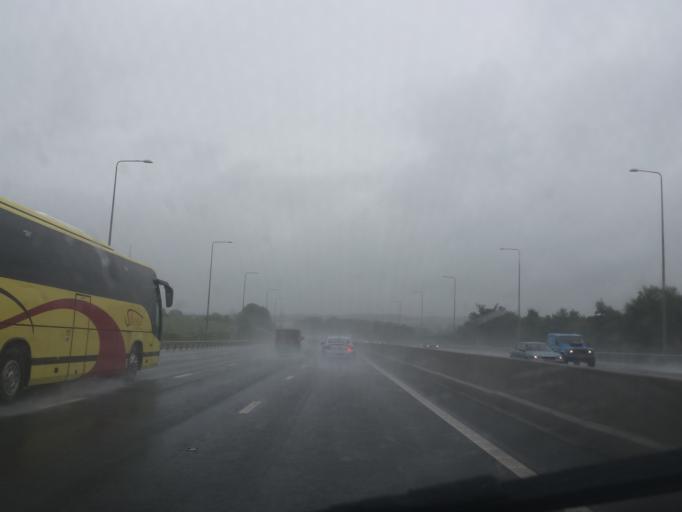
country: GB
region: England
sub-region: Nottinghamshire
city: Kimberley
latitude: 52.9549
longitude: -1.2746
